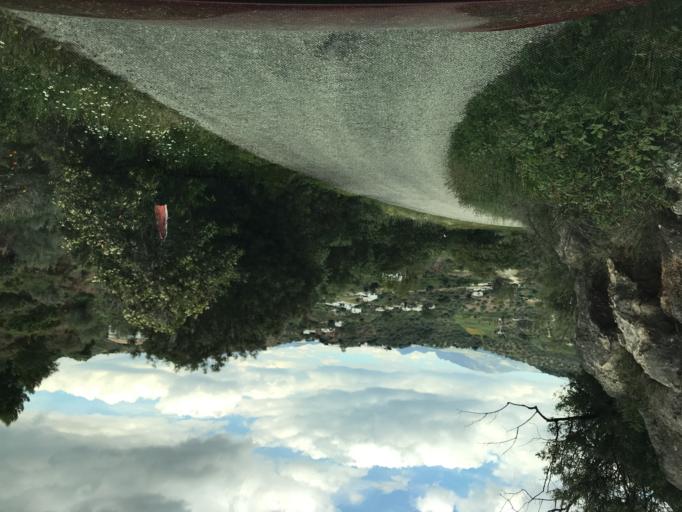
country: ES
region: Andalusia
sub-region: Provincia de Malaga
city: Comares
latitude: 36.8758
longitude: -4.2624
